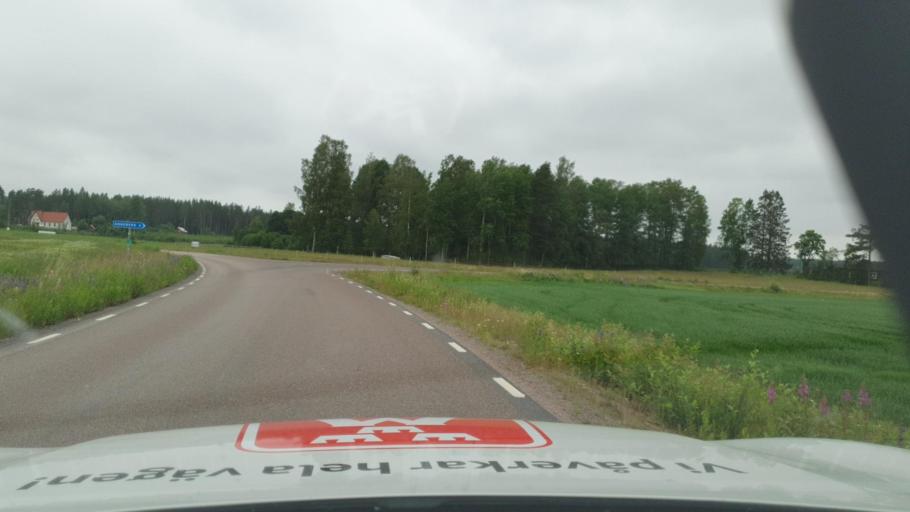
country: SE
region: Vaermland
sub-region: Kristinehamns Kommun
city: Kristinehamn
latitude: 59.4459
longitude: 13.9489
